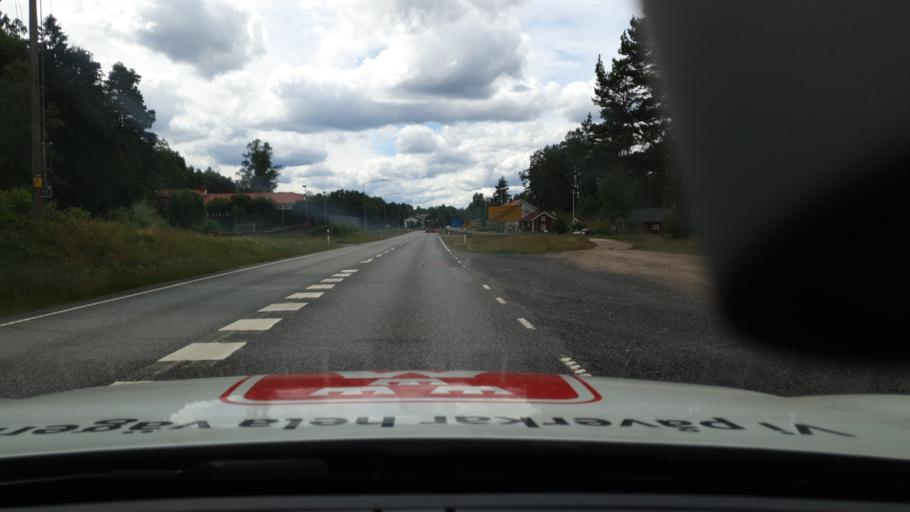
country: SE
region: Joenkoeping
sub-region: Mullsjo Kommun
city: Mullsjoe
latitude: 57.7307
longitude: 13.8729
